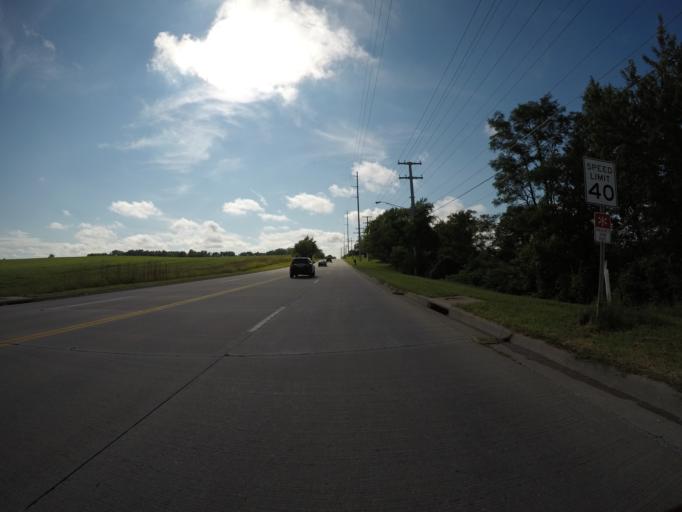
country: US
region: Kansas
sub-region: Wyandotte County
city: Edwardsville
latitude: 39.1287
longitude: -94.8464
